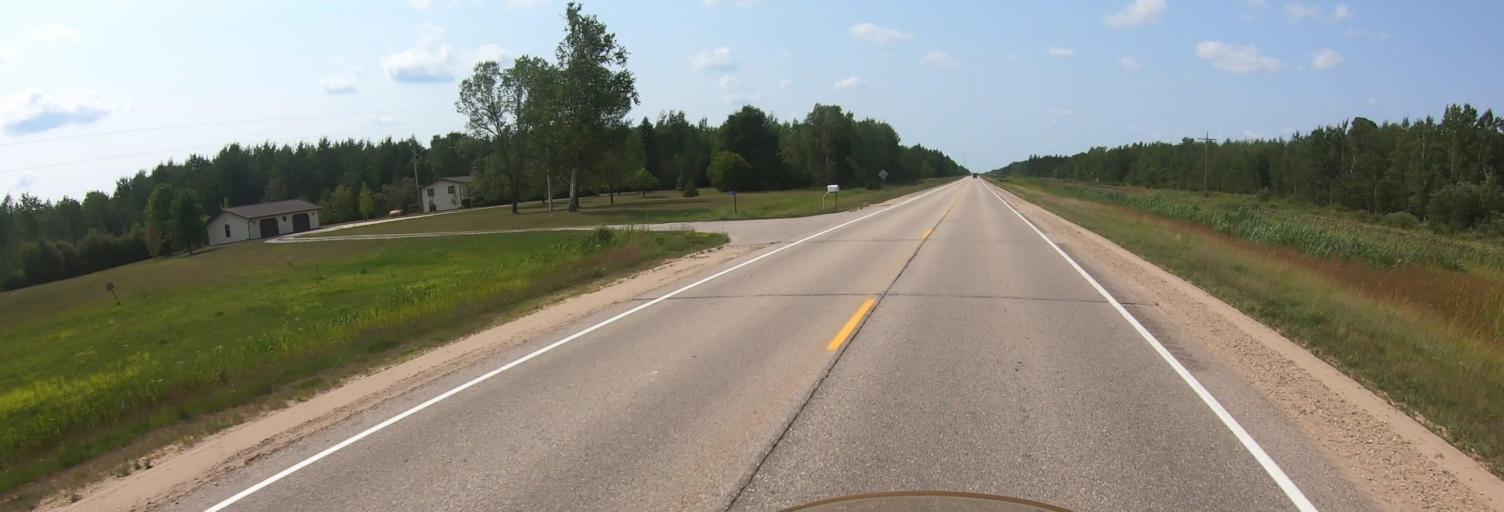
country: US
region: Minnesota
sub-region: Roseau County
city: Warroad
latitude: 48.7788
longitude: -95.0039
